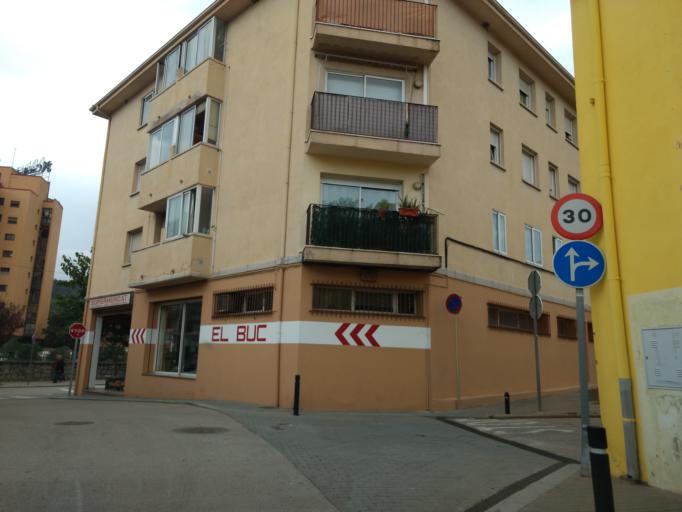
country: ES
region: Catalonia
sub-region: Provincia de Girona
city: la Jonquera
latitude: 42.4198
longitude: 2.8733
